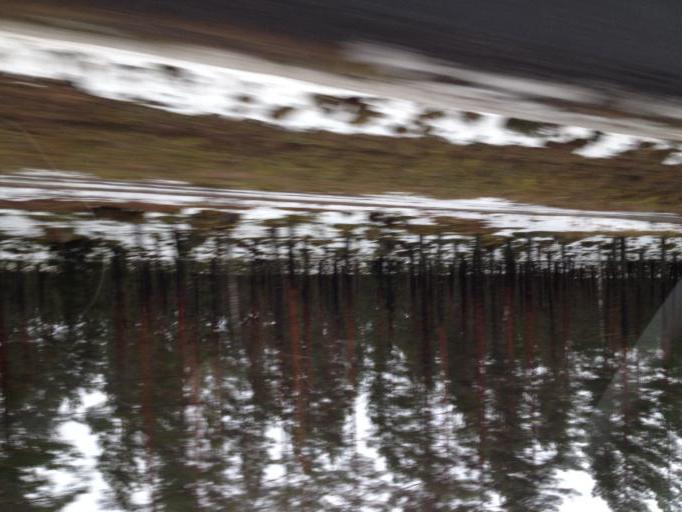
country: FI
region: Uusimaa
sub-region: Raaseporin
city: Ekenaes
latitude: 59.9102
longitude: 23.2644
